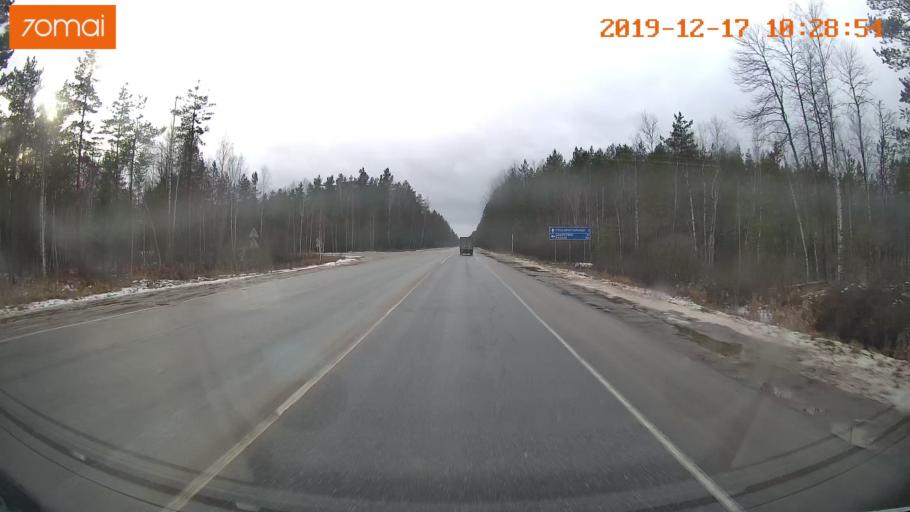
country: RU
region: Vladimir
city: Anopino
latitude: 55.6578
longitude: 40.7271
